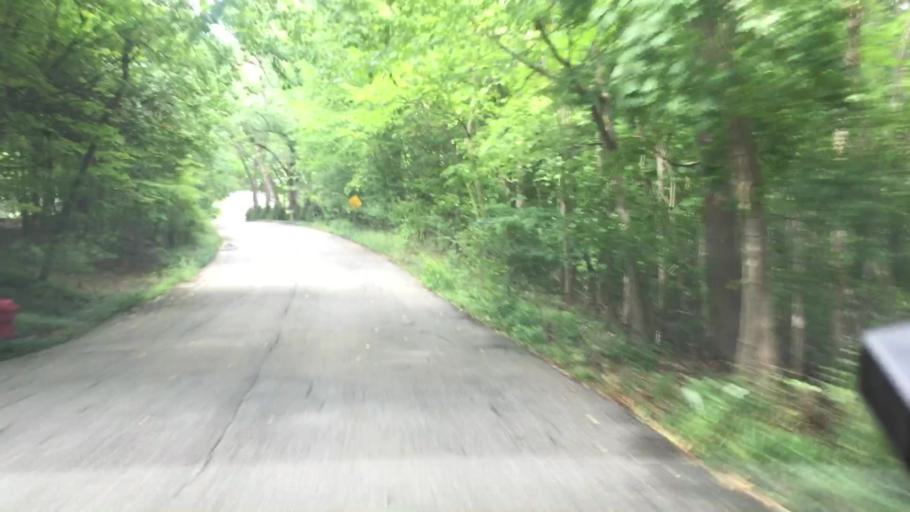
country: US
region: Michigan
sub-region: Oakland County
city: Sylvan Lake
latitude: 42.5713
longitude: -83.3184
